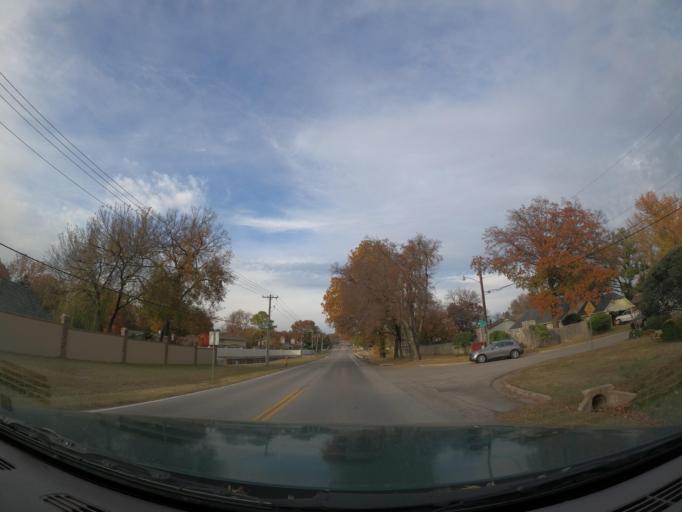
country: US
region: Oklahoma
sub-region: Tulsa County
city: Jenks
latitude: 36.0570
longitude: -95.9401
